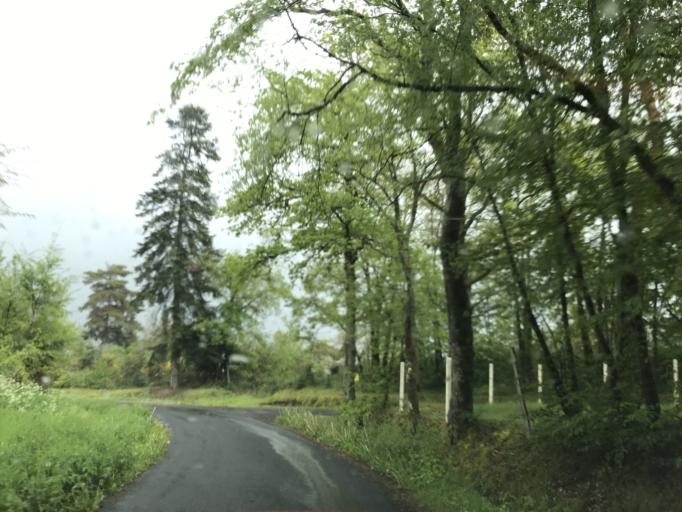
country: FR
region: Auvergne
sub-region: Departement du Puy-de-Dome
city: Courpiere
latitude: 45.7470
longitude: 3.5262
